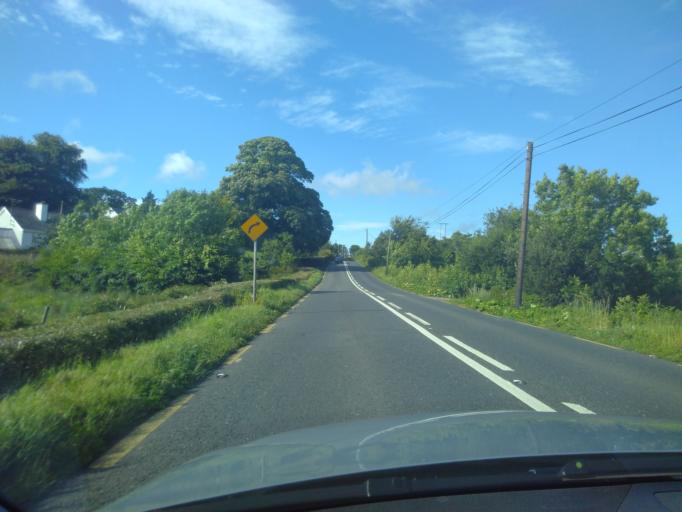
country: IE
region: Ulster
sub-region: County Donegal
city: Ballybofey
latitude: 54.8181
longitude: -7.7572
